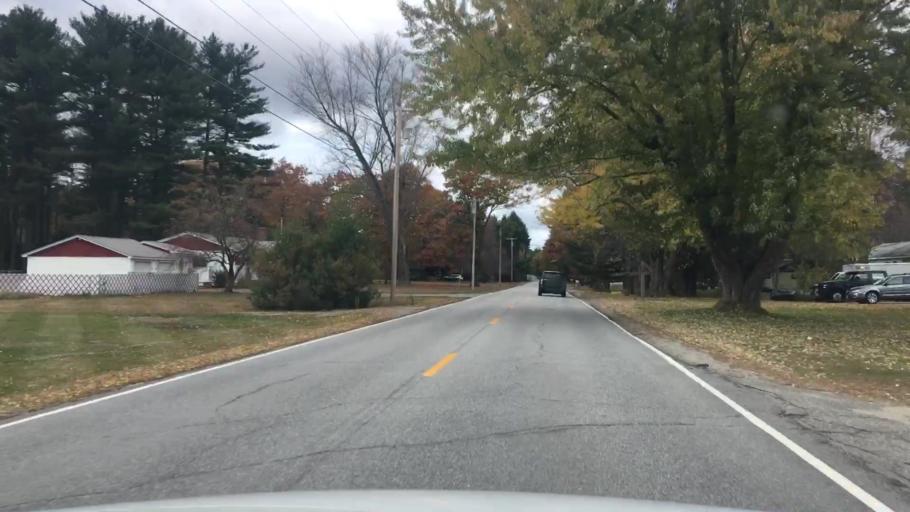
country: US
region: Maine
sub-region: Kennebec County
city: Monmouth
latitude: 44.2302
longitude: -70.0821
